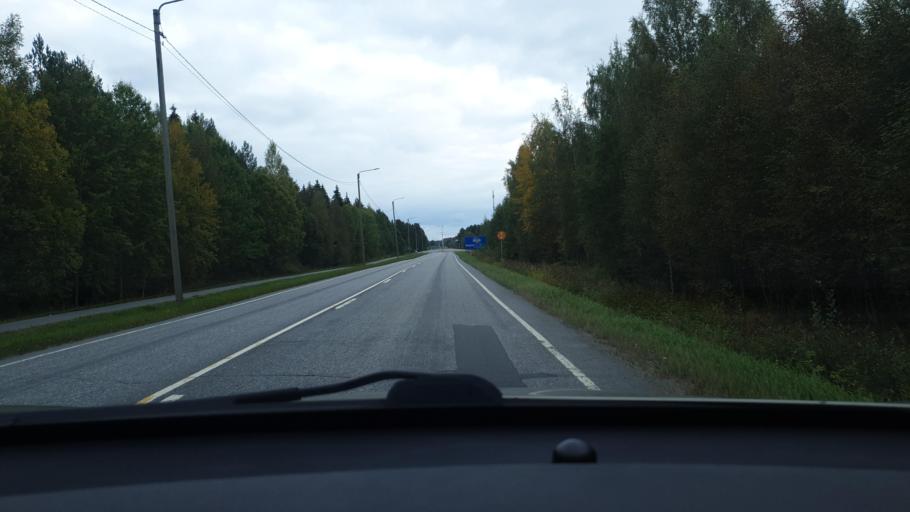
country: FI
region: Ostrobothnia
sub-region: Vaasa
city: Ristinummi
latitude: 63.0573
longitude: 21.7152
